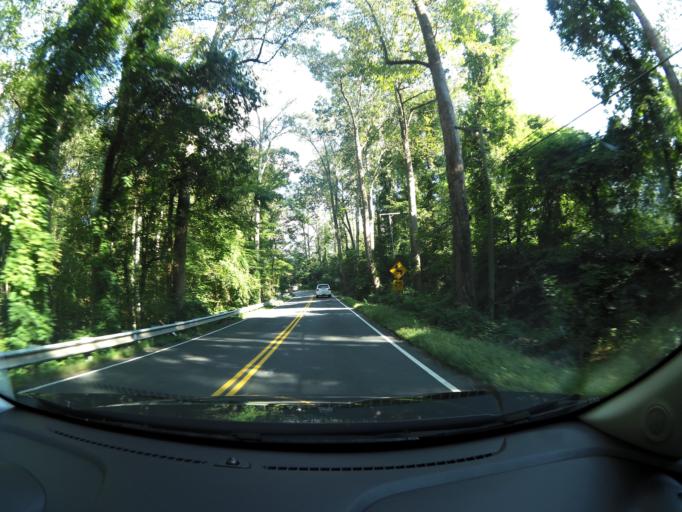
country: US
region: Virginia
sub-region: Fairfax County
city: Tysons Corner
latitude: 38.9600
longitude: -77.2182
